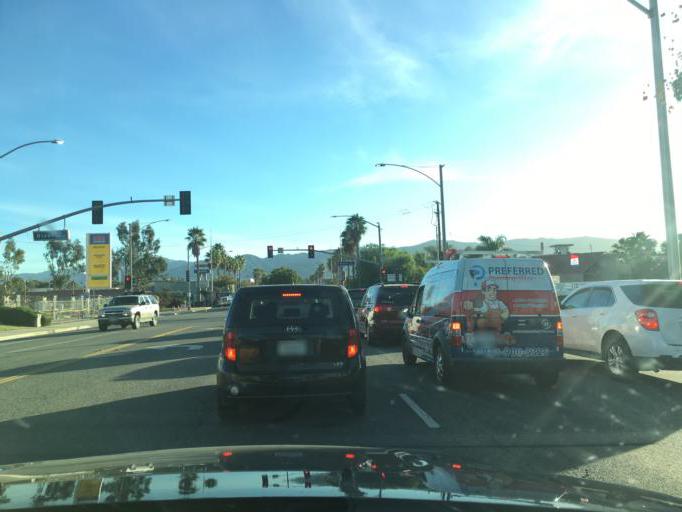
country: US
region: California
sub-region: Riverside County
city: Corona
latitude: 33.8887
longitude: -117.5644
